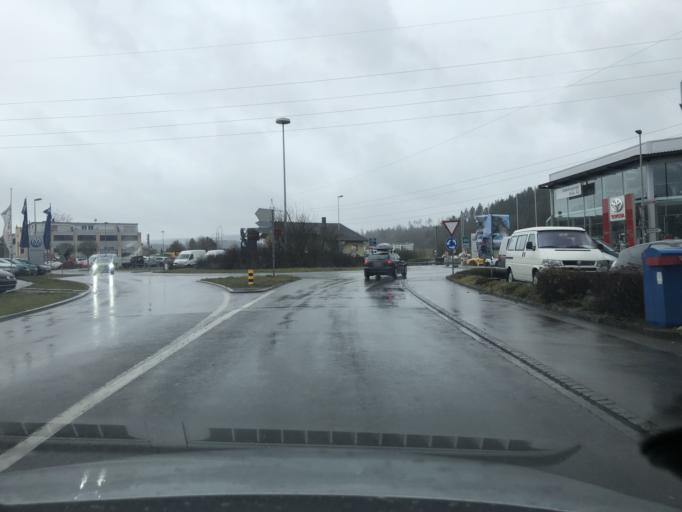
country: CH
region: Aargau
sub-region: Bezirk Brugg
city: Hausen
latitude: 47.4706
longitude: 8.2104
